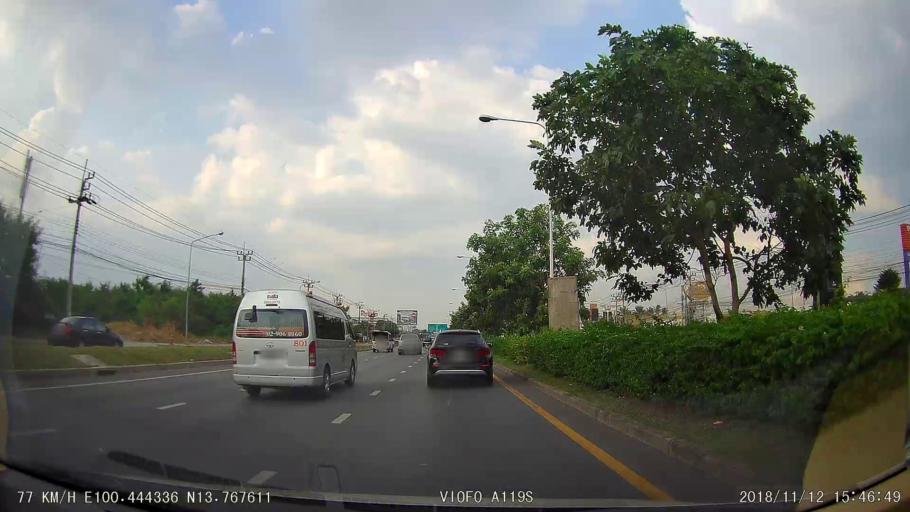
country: TH
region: Bangkok
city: Taling Chan
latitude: 13.7678
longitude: 100.4443
